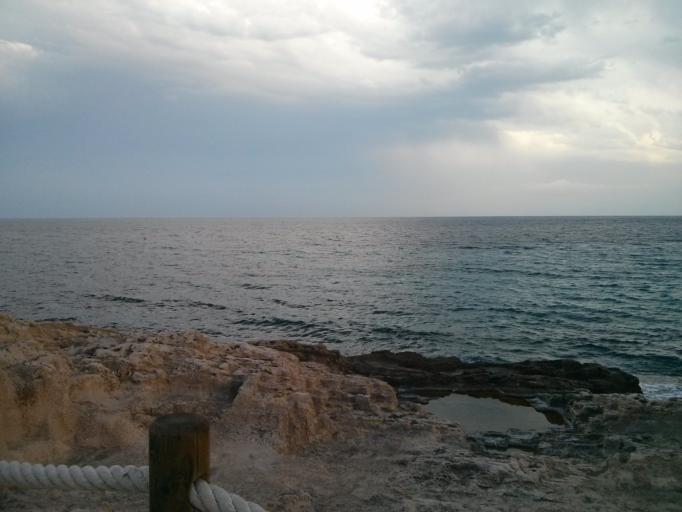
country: ES
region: Valencia
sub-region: Provincia de Alicante
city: Moraira
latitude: 38.6866
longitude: 0.1319
